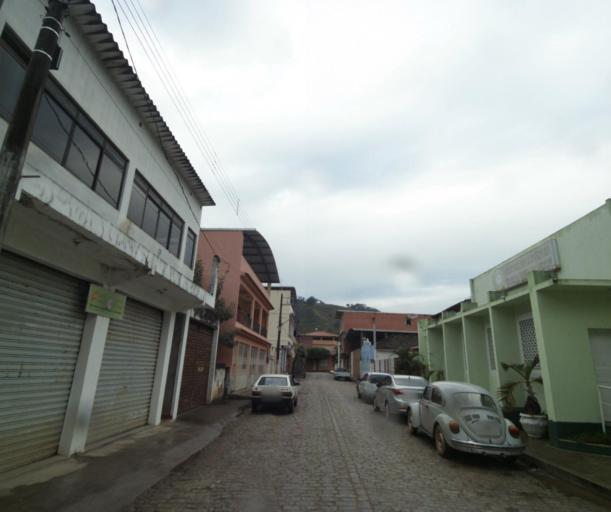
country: BR
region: Espirito Santo
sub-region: Muniz Freire
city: Muniz Freire
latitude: -20.4619
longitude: -41.4158
